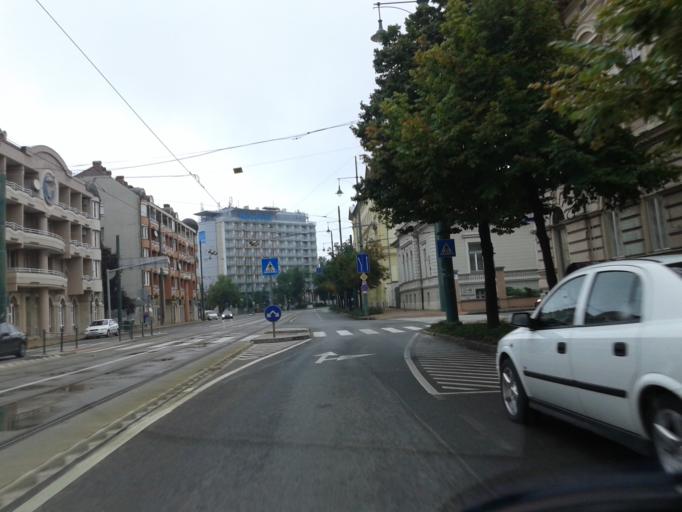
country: HU
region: Csongrad
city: Szeged
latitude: 46.2565
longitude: 20.1540
